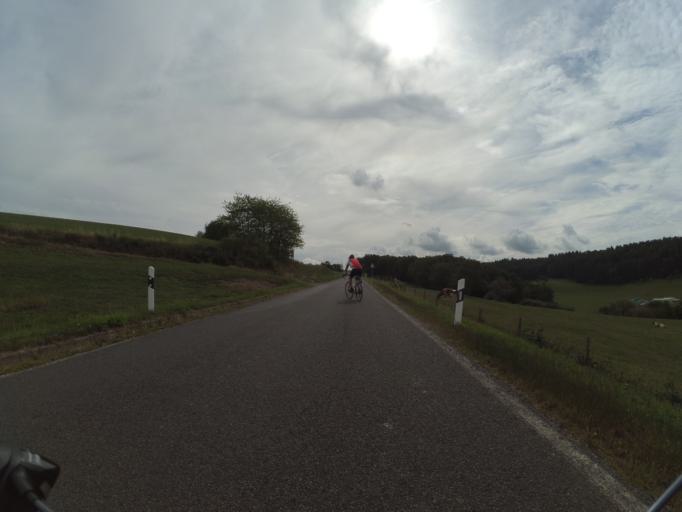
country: DE
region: Rheinland-Pfalz
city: Gladbach
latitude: 49.9309
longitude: 6.7699
